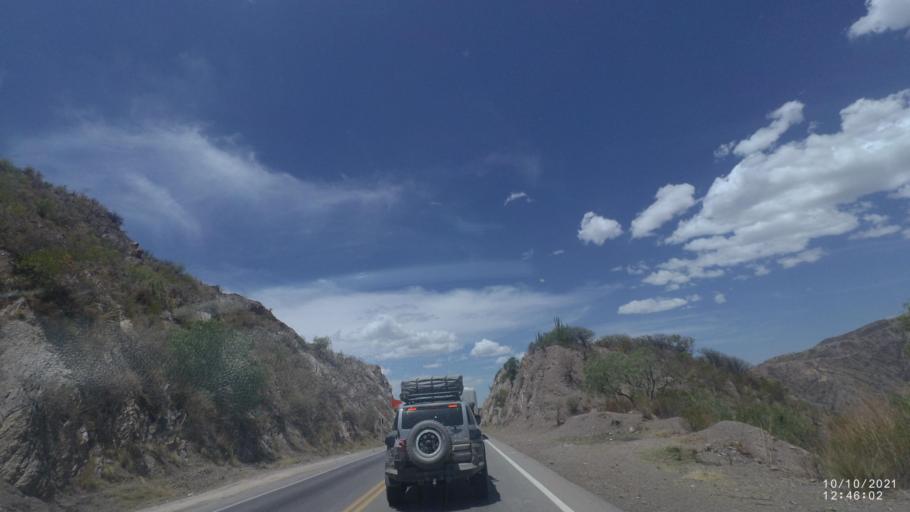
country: BO
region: Cochabamba
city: Irpa Irpa
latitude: -17.6346
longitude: -66.3663
